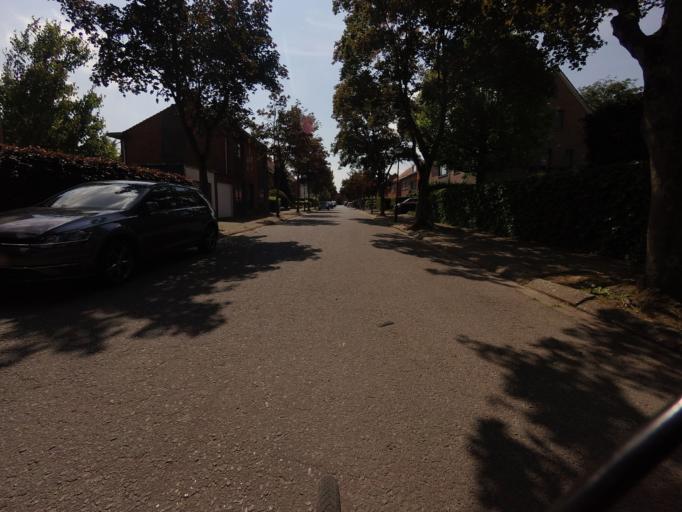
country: BE
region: Flanders
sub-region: Provincie Antwerpen
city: Hove
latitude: 51.1667
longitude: 4.4761
